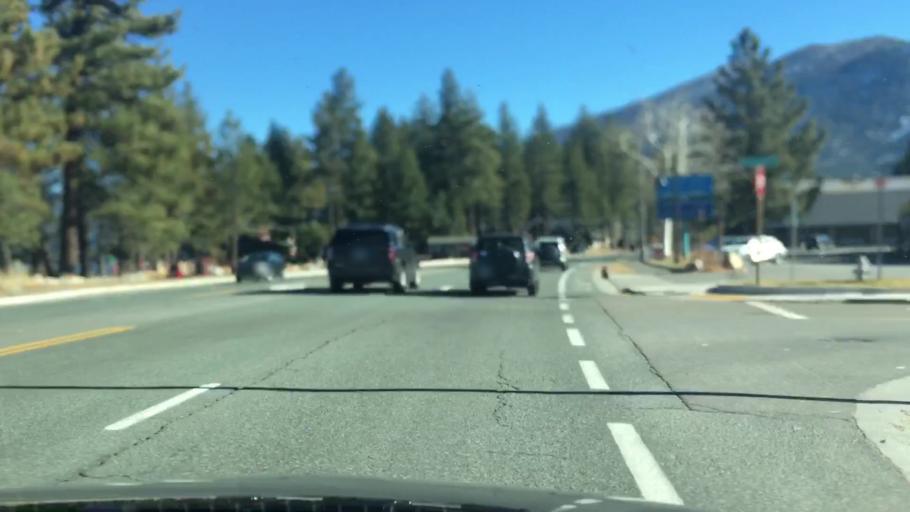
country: US
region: California
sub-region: El Dorado County
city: South Lake Tahoe
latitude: 38.9456
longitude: -119.9711
